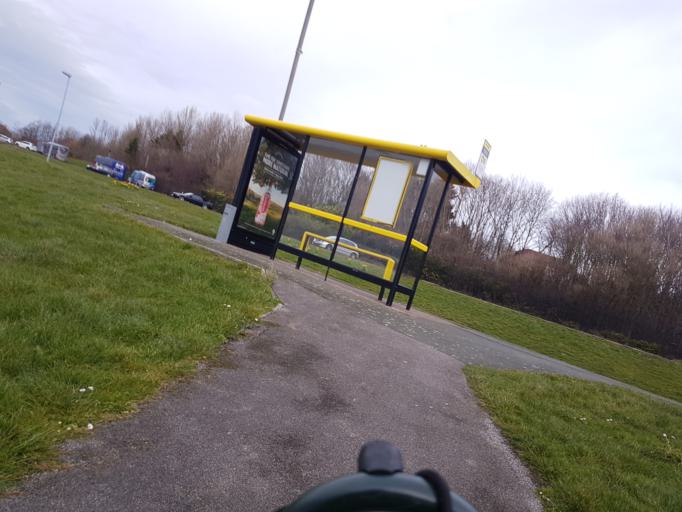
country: GB
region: England
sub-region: Metropolitan Borough of Wirral
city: Bromborough
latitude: 53.3743
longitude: -2.9649
